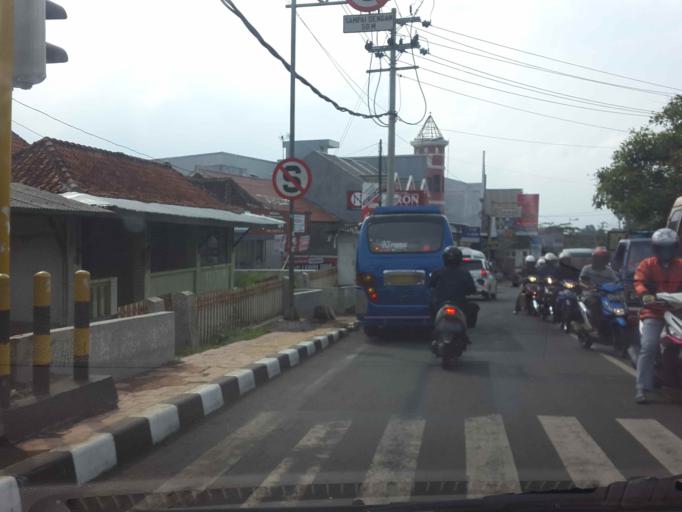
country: ID
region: Central Java
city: Salatiga
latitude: -7.3222
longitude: 110.4964
